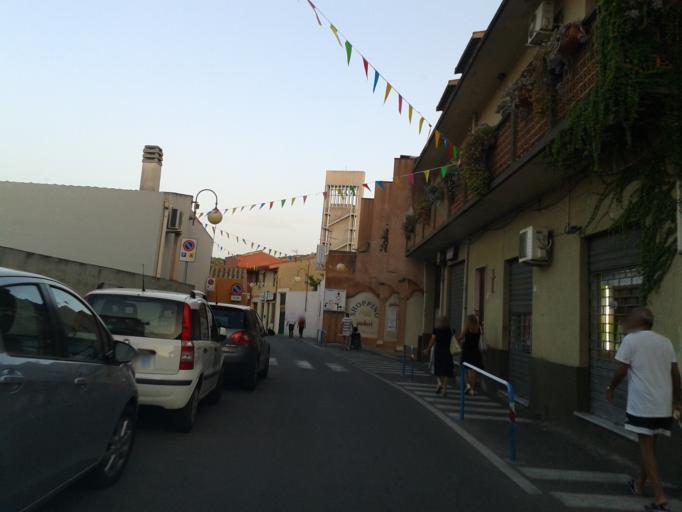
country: IT
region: Sardinia
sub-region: Provincia di Cagliari
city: Villasimius
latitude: 39.1432
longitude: 9.5187
